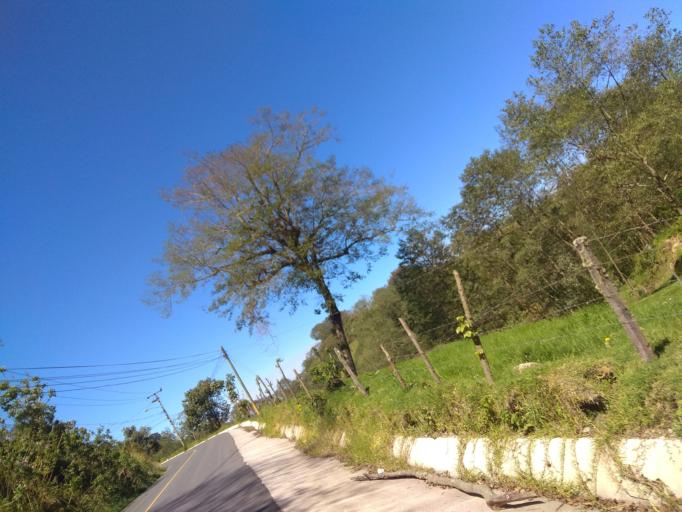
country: CR
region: Cartago
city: Concepcion
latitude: 9.9528
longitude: -83.9295
